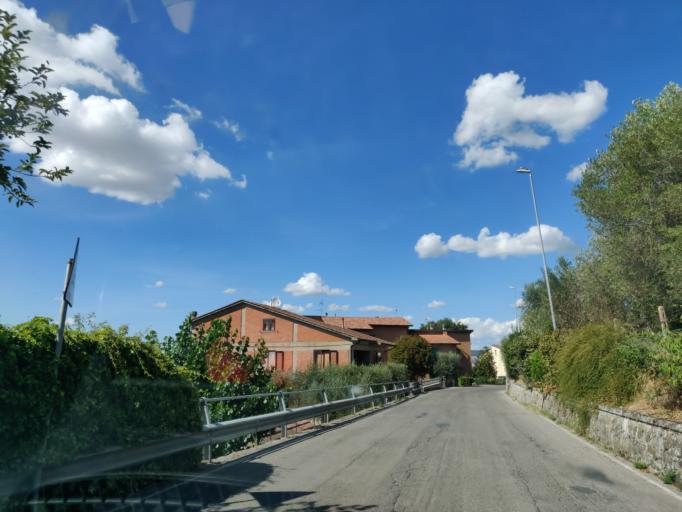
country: IT
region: Tuscany
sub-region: Provincia di Siena
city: Radicofani
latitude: 42.9745
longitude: 11.7387
